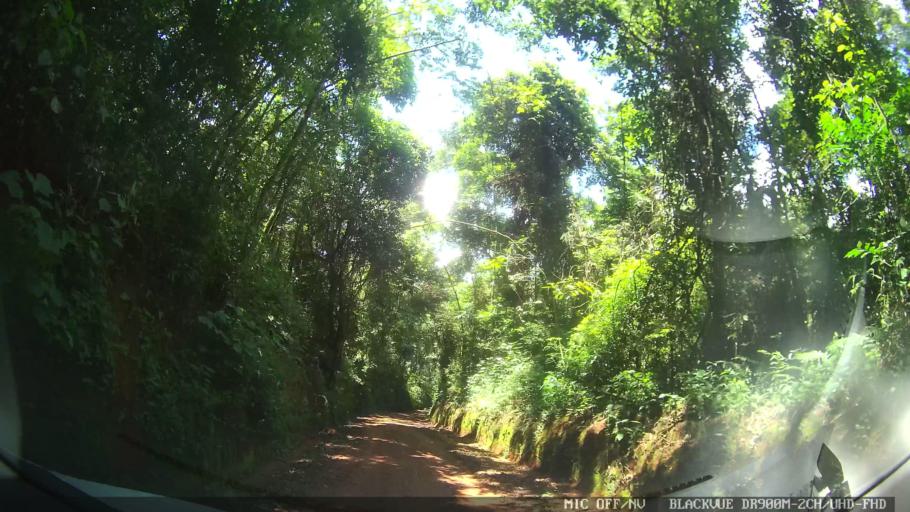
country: BR
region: Sao Paulo
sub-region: Joanopolis
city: Joanopolis
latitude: -22.8955
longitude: -46.2987
